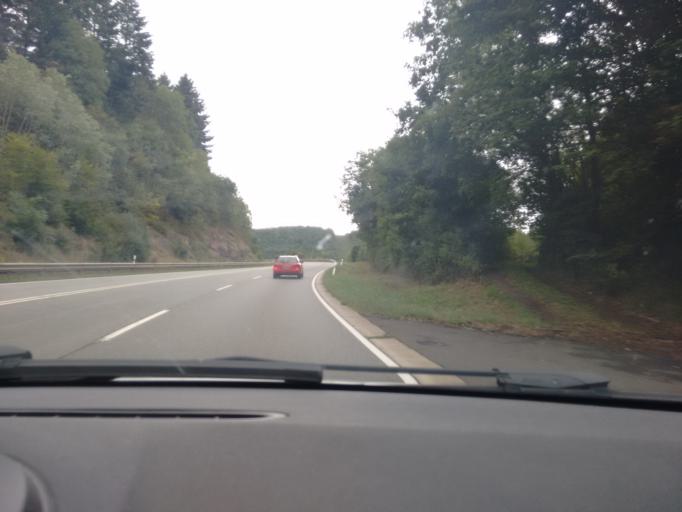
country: DE
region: Rheinland-Pfalz
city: Idar-Oberstein
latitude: 49.6987
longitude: 7.3120
